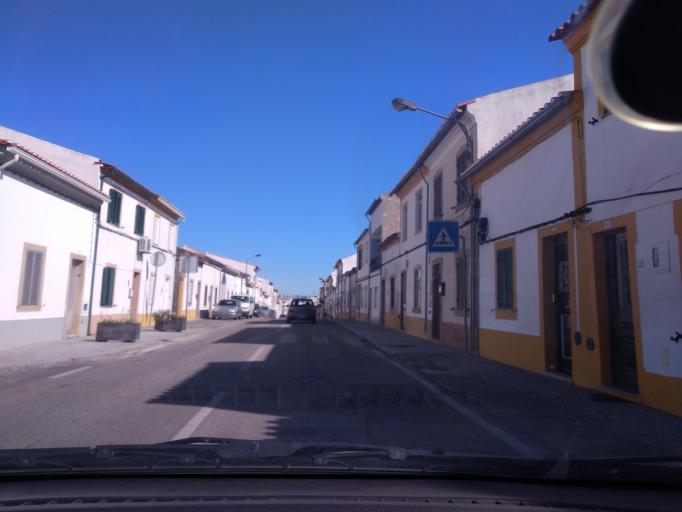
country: PT
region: Portalegre
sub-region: Nisa
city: Nisa
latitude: 39.5095
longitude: -7.6460
